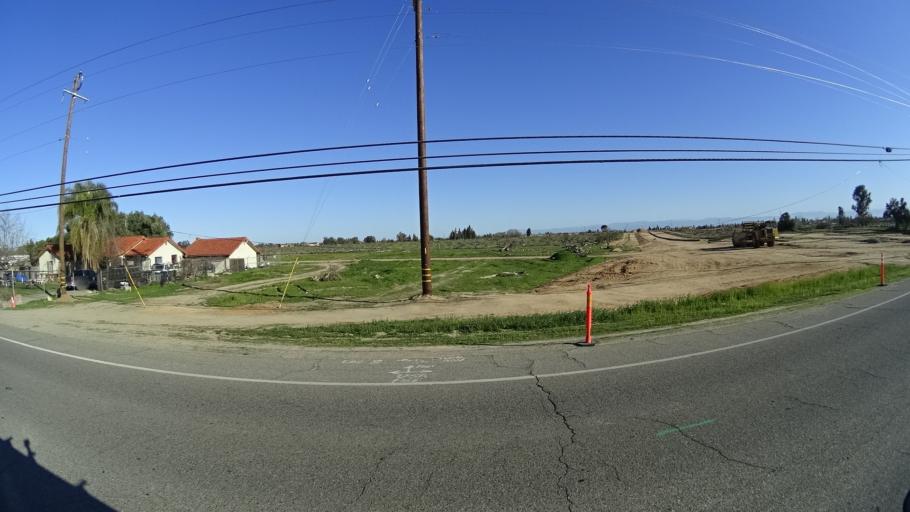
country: US
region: California
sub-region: Fresno County
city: Biola
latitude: 36.8079
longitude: -119.9117
